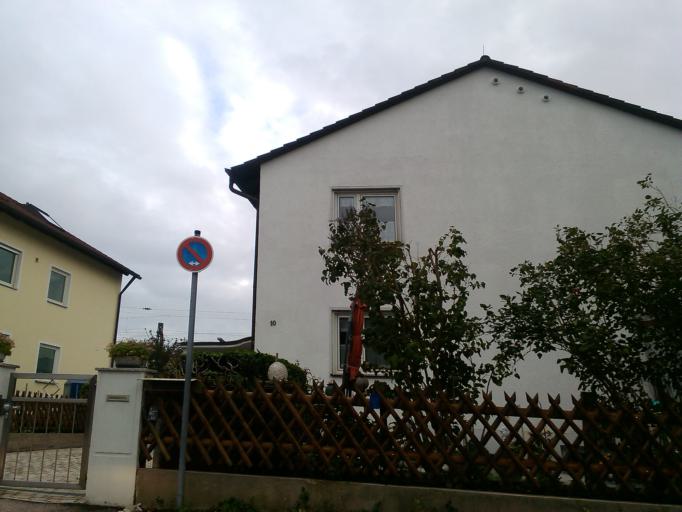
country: DE
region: Bavaria
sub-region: Upper Bavaria
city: Grobenzell
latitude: 48.1932
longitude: 11.3761
